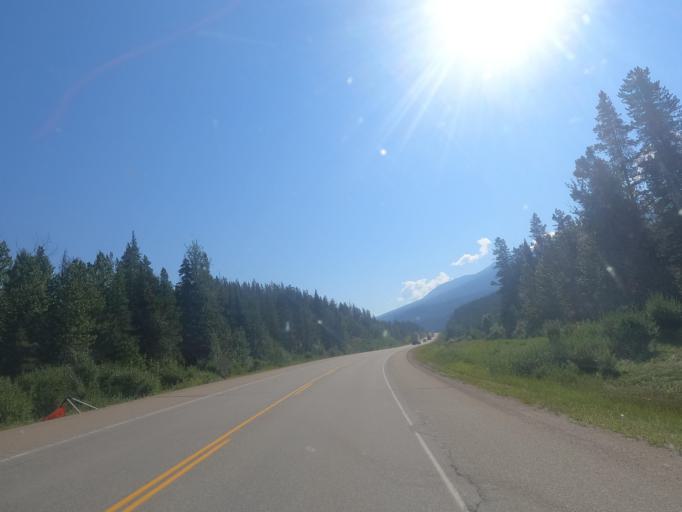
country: CA
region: Alberta
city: Jasper Park Lodge
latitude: 52.8878
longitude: -118.4734
